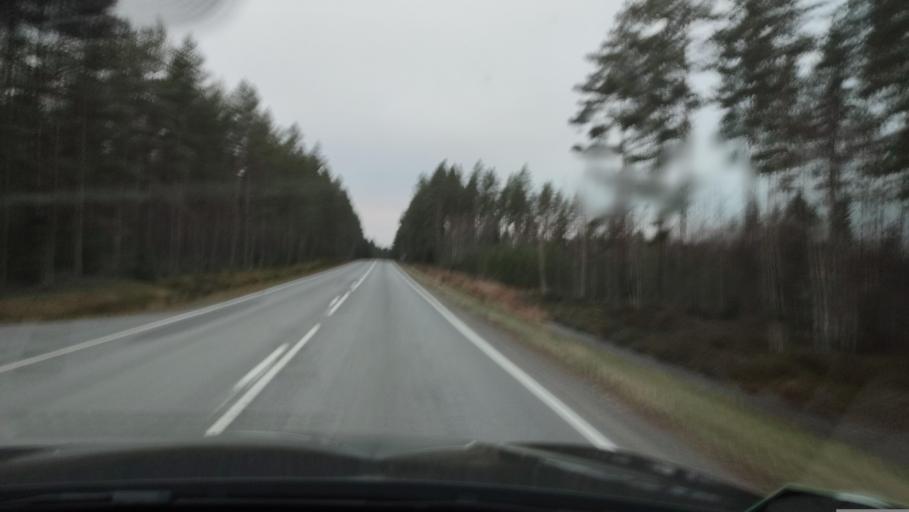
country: FI
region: Southern Ostrobothnia
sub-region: Suupohja
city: Karijoki
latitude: 62.3235
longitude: 21.7649
